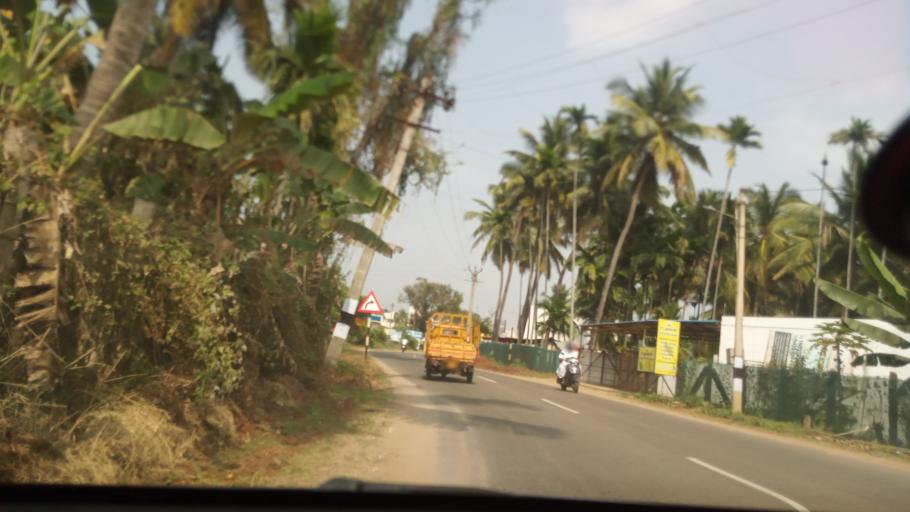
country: IN
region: Tamil Nadu
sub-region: Coimbatore
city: Perur
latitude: 11.0027
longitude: 76.8602
